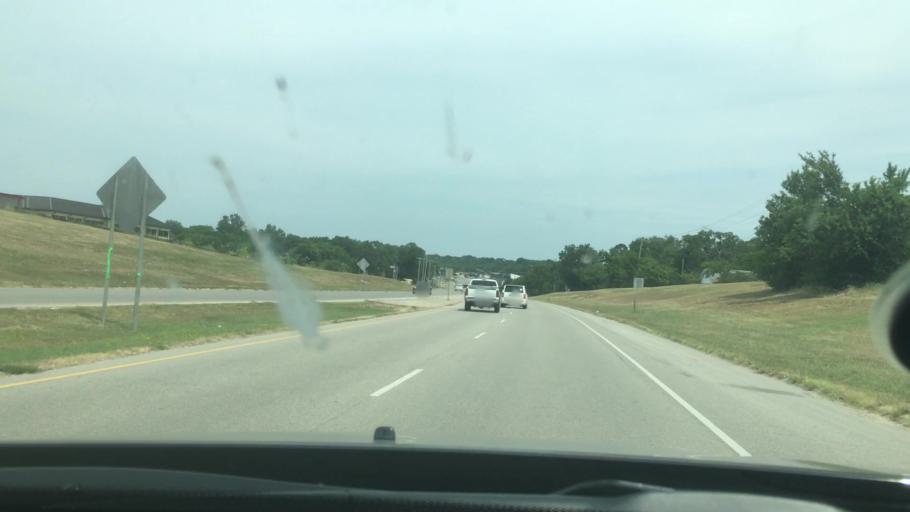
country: US
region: Oklahoma
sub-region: Pontotoc County
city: Ada
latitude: 34.7544
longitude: -96.6582
